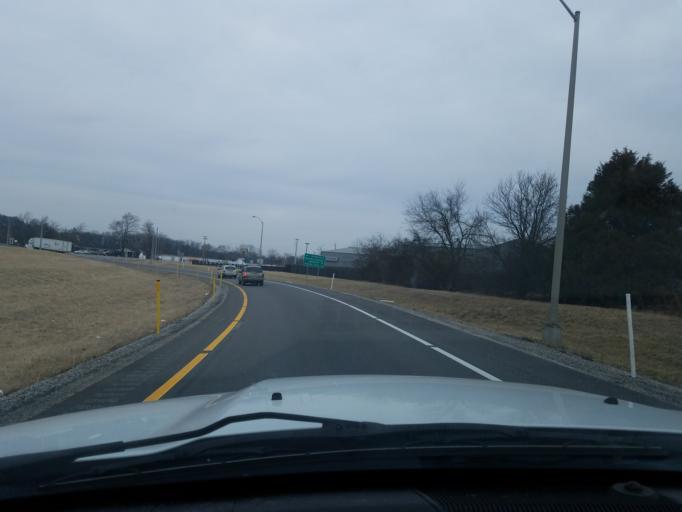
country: US
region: Kentucky
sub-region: Warren County
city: Bowling Green
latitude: 36.9563
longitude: -86.4955
